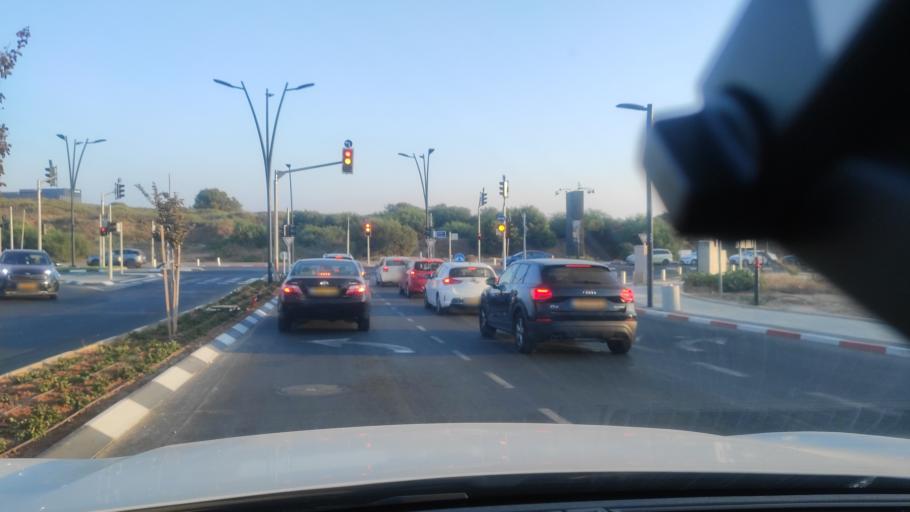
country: IL
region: Tel Aviv
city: Herzliya Pituah
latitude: 32.1644
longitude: 34.8027
